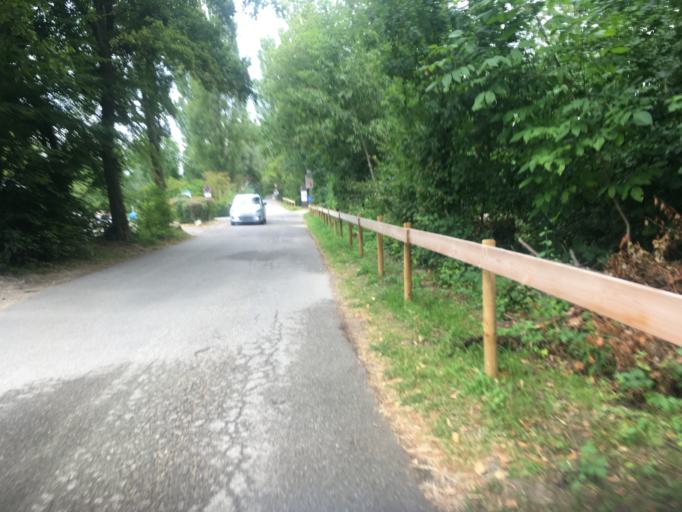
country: CH
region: Bern
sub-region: Seeland District
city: Erlach
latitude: 47.0461
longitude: 7.1007
